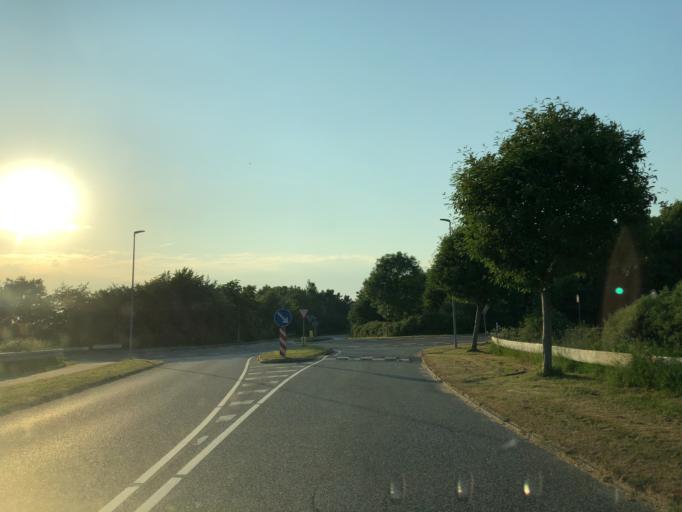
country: DK
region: Central Jutland
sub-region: Struer Kommune
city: Struer
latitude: 56.4879
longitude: 8.5619
